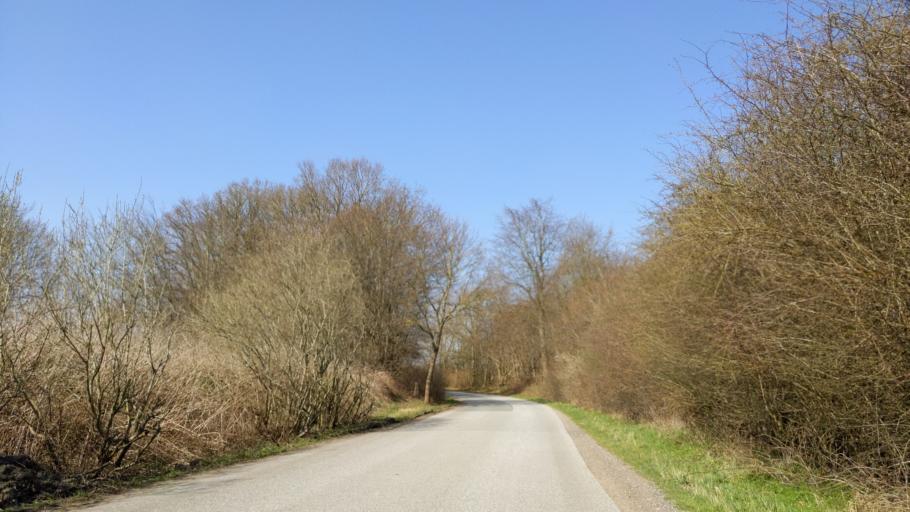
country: DE
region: Schleswig-Holstein
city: Susel
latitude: 54.0915
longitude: 10.7128
